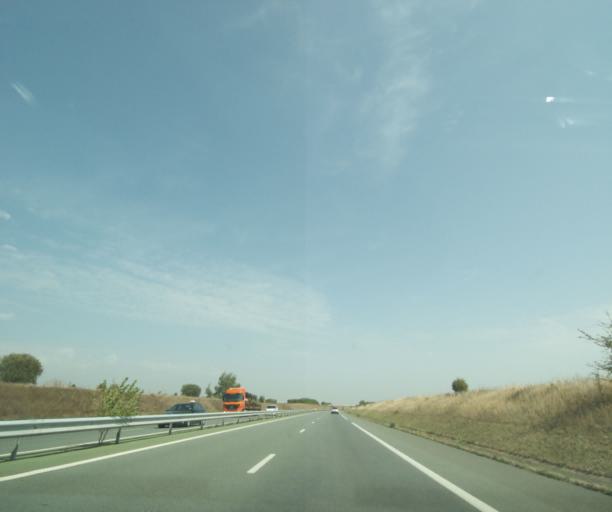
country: FR
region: Poitou-Charentes
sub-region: Departement des Deux-Sevres
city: Villiers-en-Plaine
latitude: 46.4167
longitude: -0.5633
